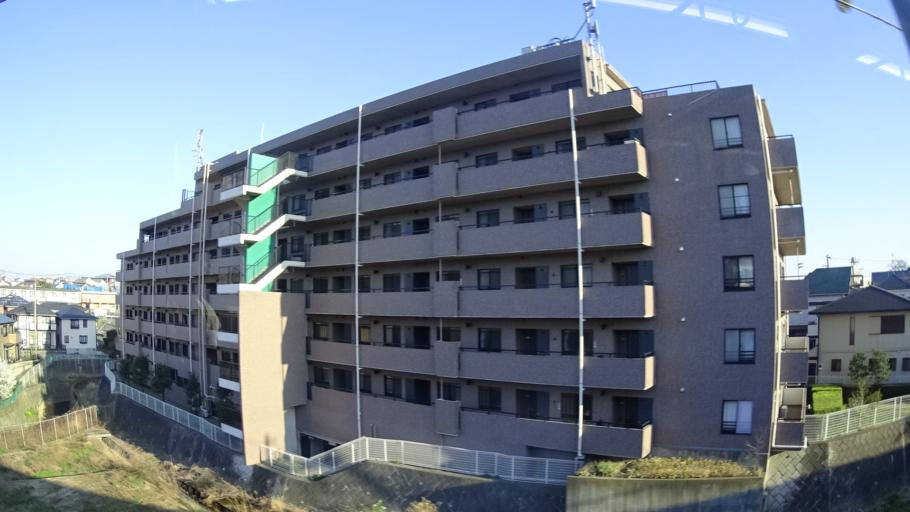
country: JP
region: Kanagawa
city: Yokosuka
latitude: 35.2095
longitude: 139.6829
